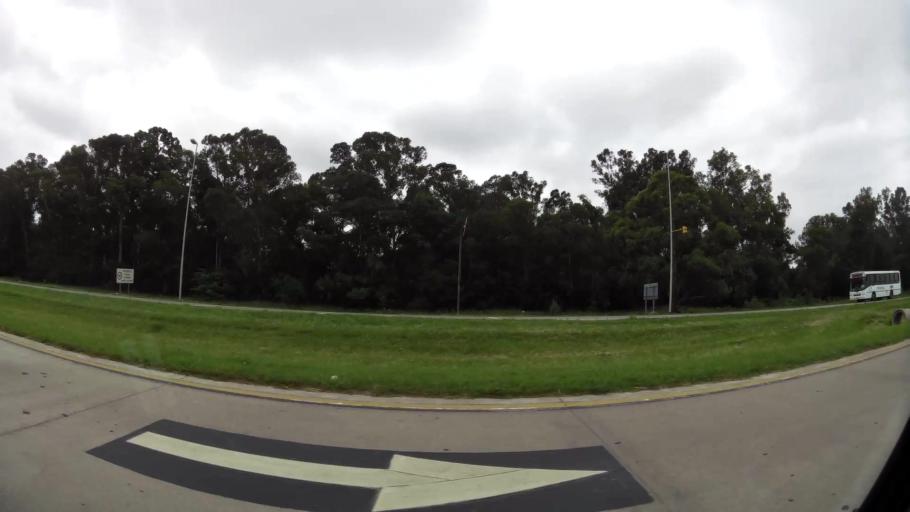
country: AR
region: Buenos Aires
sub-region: Partido de San Vicente
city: San Vicente
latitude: -35.0541
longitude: -58.4394
